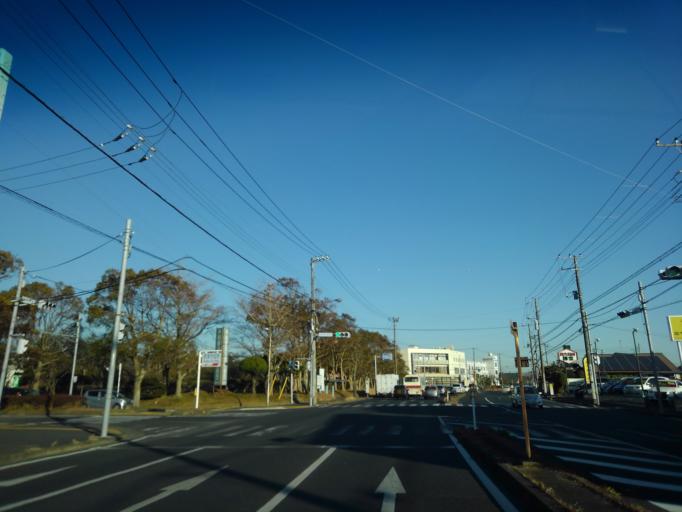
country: JP
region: Chiba
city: Kimitsu
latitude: 35.3292
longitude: 139.9010
